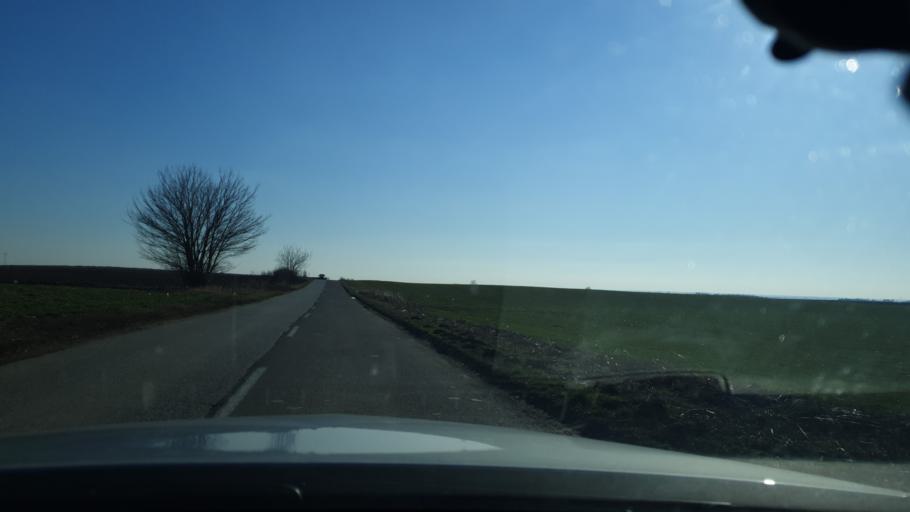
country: RS
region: Autonomna Pokrajina Vojvodina
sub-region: Sremski Okrug
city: Ruma
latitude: 45.0619
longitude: 19.8083
